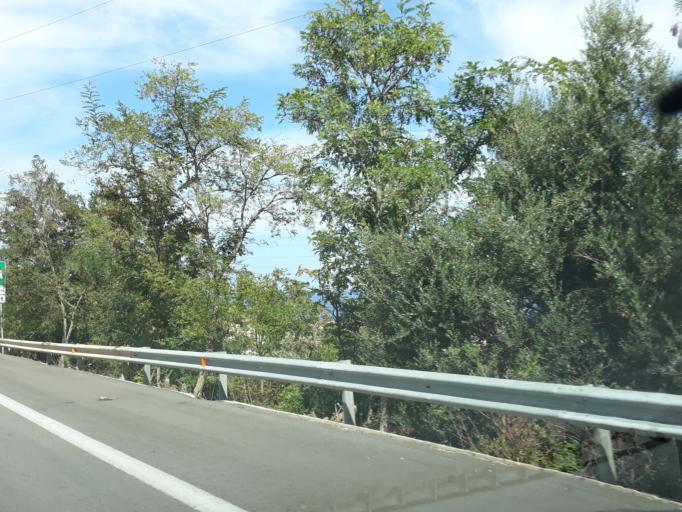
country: IT
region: Sicily
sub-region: Palermo
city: Trabia
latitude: 37.9848
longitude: 13.6583
